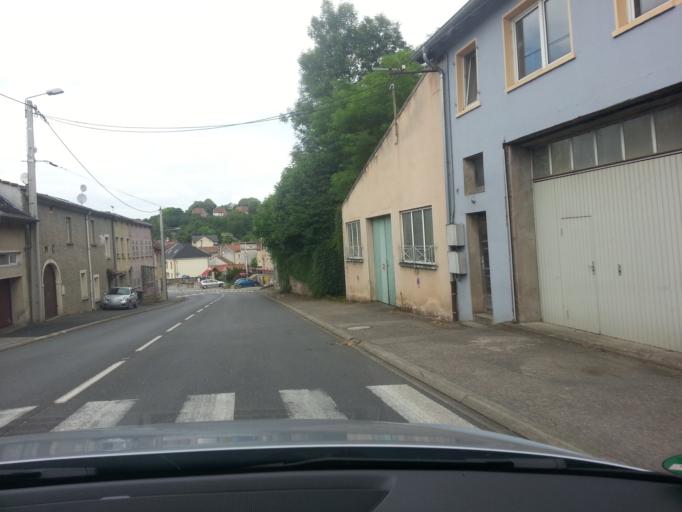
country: DE
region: Saarland
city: Perl
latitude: 49.4582
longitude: 6.3744
